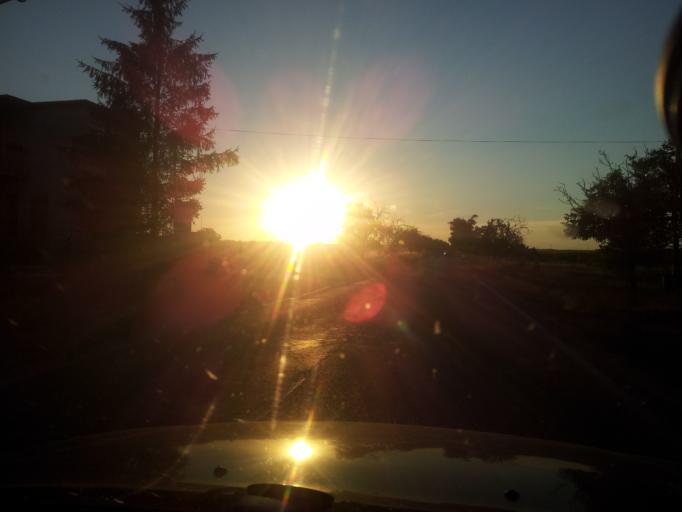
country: SK
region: Nitriansky
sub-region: Okres Nove Zamky
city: Sturovo
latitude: 47.8567
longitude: 18.6491
